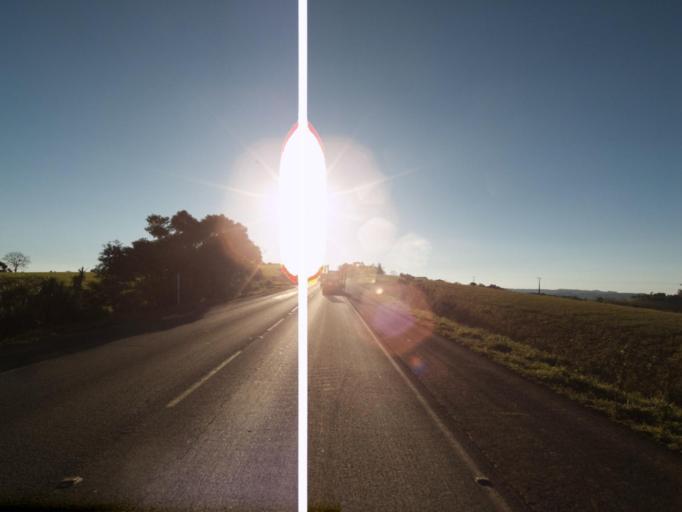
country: BR
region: Santa Catarina
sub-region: Chapeco
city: Chapeco
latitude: -26.8734
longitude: -52.9559
